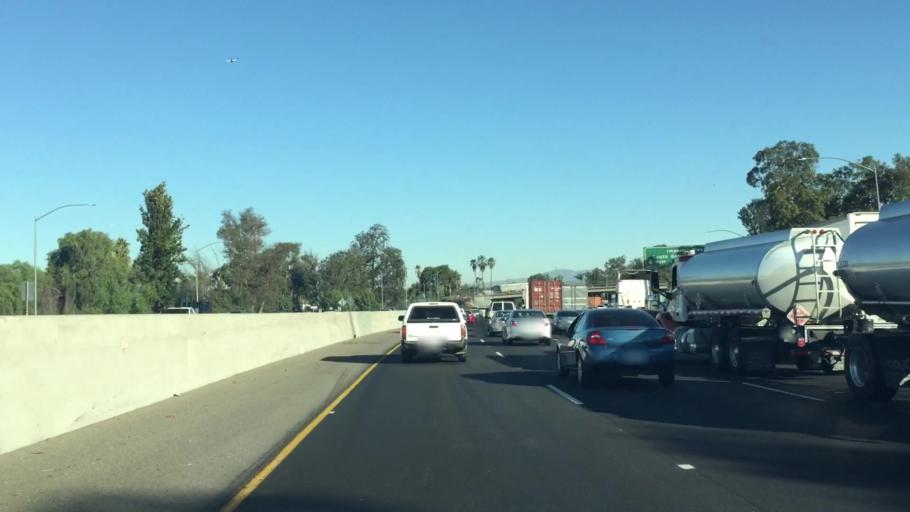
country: US
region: California
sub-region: Los Angeles County
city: Lynwood
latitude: 33.9280
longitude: -118.1785
